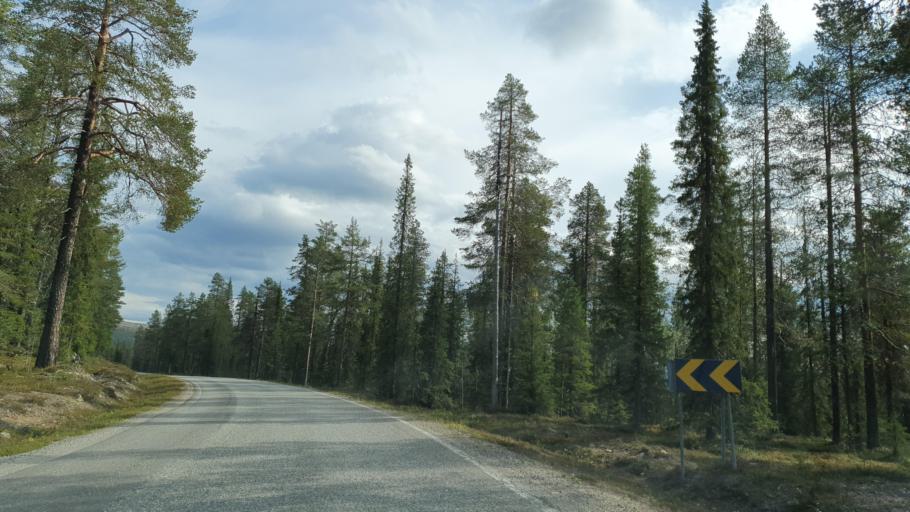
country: FI
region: Lapland
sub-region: Tunturi-Lappi
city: Kolari
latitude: 67.6709
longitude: 24.1499
